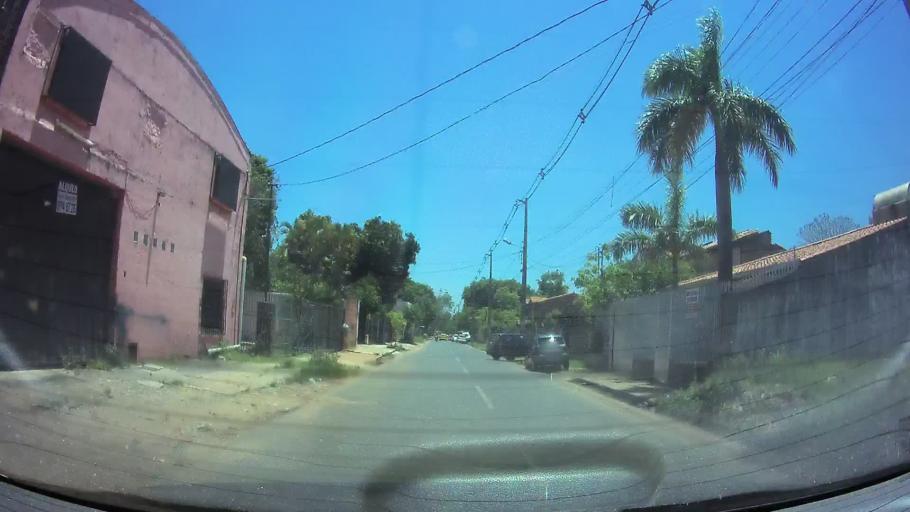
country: PY
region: Central
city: Fernando de la Mora
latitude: -25.2920
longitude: -57.5396
